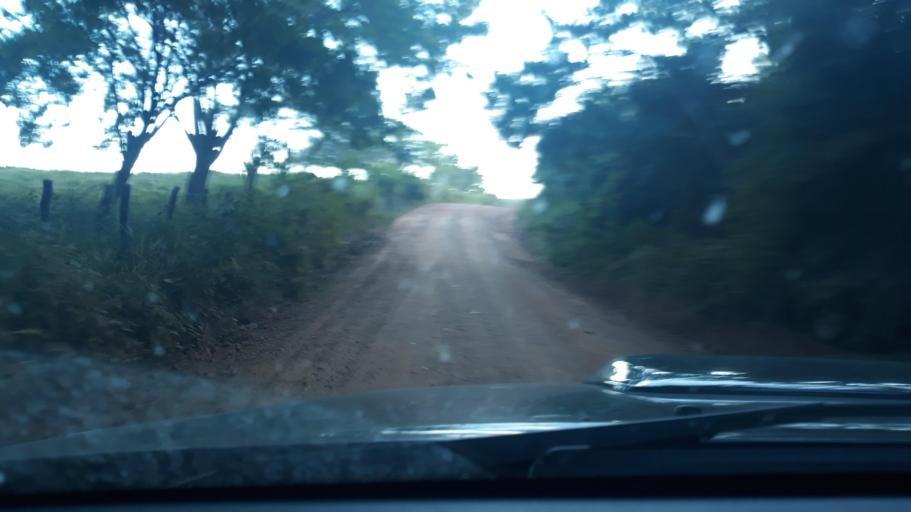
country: BR
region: Bahia
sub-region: Riacho De Santana
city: Riacho de Santana
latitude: -13.8134
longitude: -42.7215
